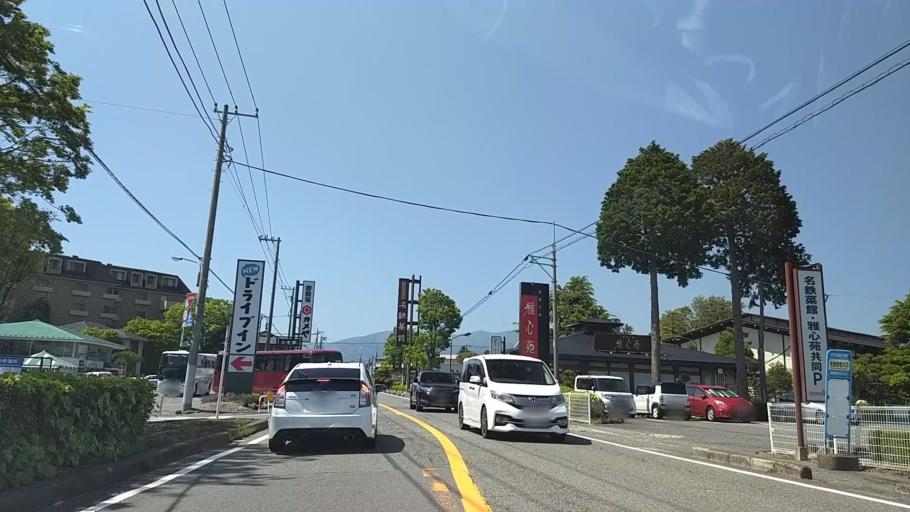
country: JP
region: Shizuoka
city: Gotemba
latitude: 35.2981
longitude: 138.9416
